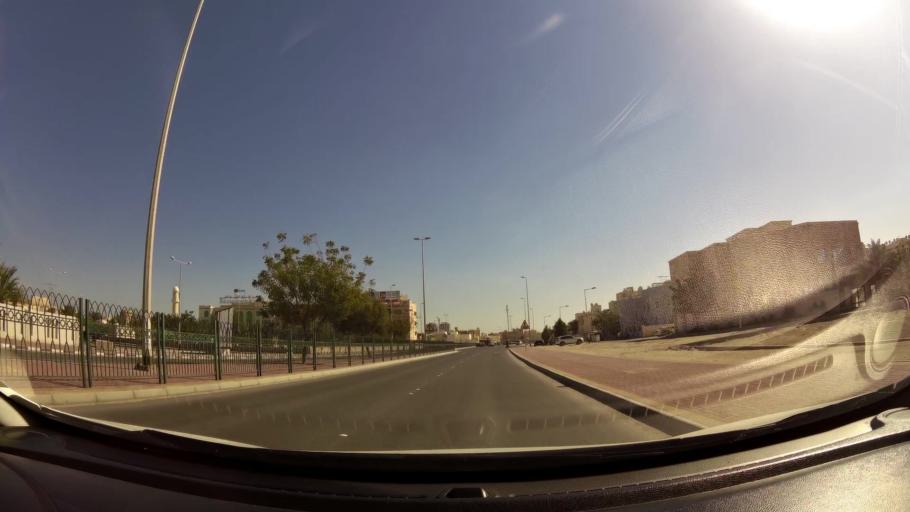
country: BH
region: Muharraq
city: Al Hadd
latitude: 26.2360
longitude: 50.6519
